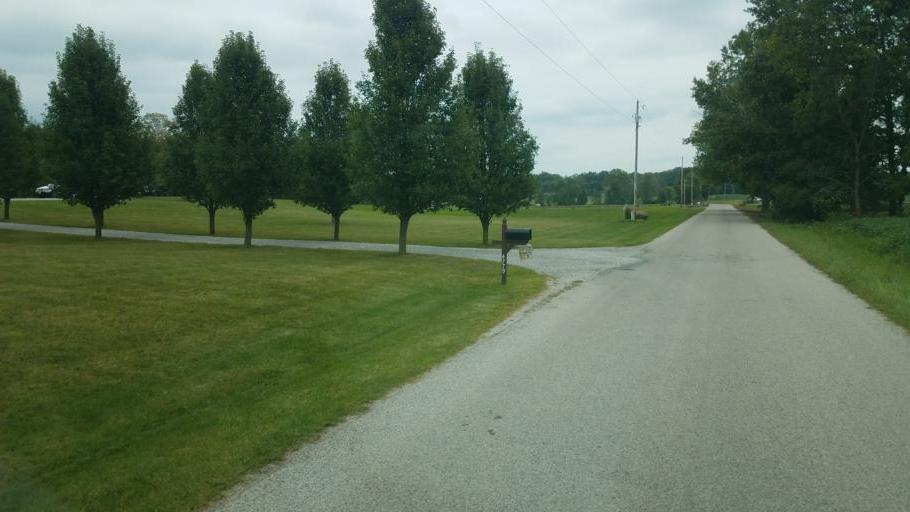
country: US
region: Ohio
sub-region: Morrow County
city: Mount Gilead
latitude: 40.5266
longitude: -82.8075
